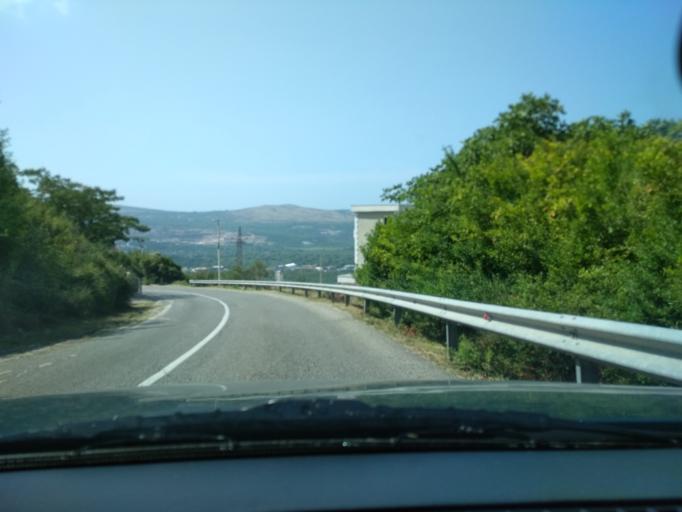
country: ME
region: Kotor
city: Kotor
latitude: 42.3980
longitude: 18.7563
